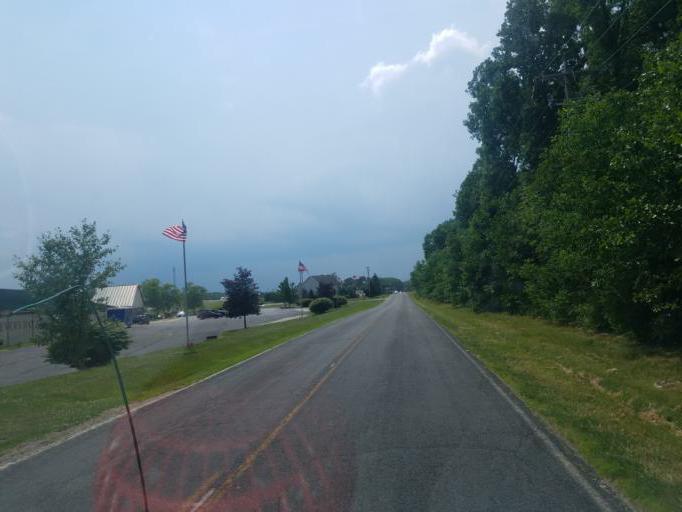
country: US
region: Ohio
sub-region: Portage County
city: Ravenna
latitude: 41.1110
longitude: -81.2361
